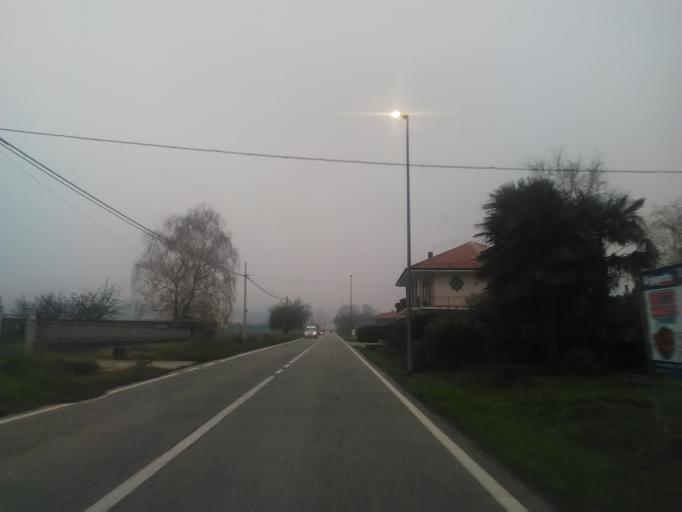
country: IT
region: Piedmont
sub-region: Provincia di Vercelli
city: Moncrivello
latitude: 45.3243
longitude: 8.0100
